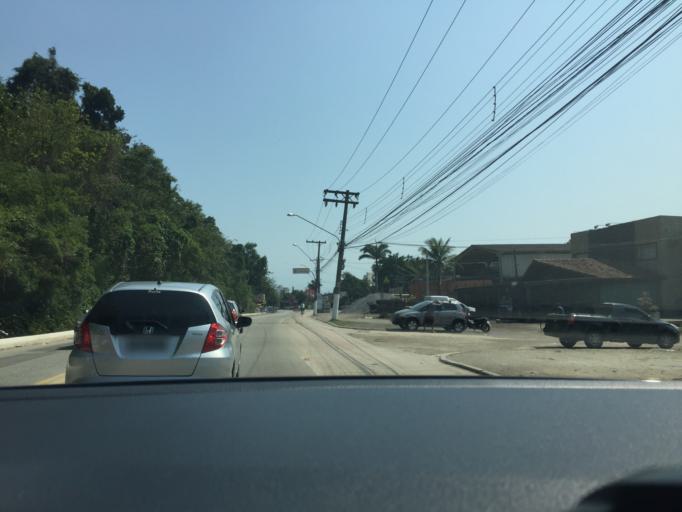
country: BR
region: Sao Paulo
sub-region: Guaruja
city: Guaruja
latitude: -23.9805
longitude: -46.1940
